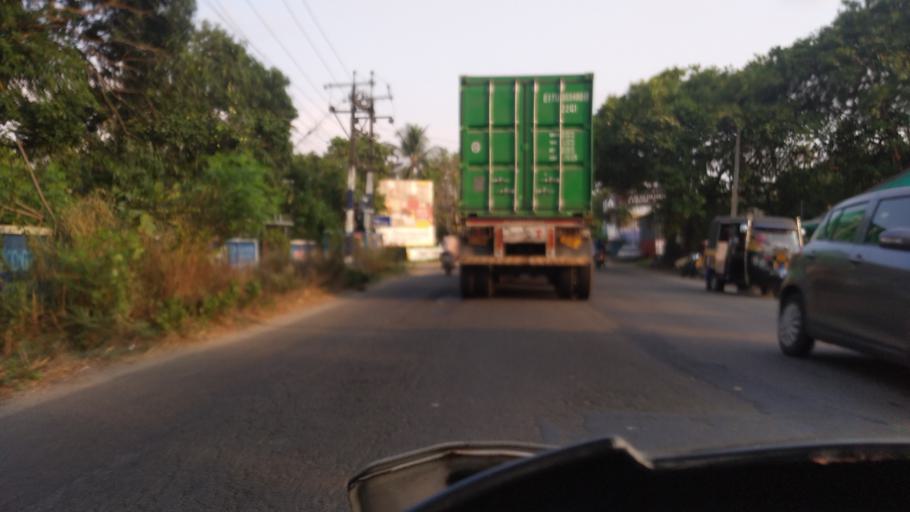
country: IN
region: Kerala
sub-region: Thrissur District
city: Irinjalakuda
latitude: 10.3374
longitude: 76.1383
